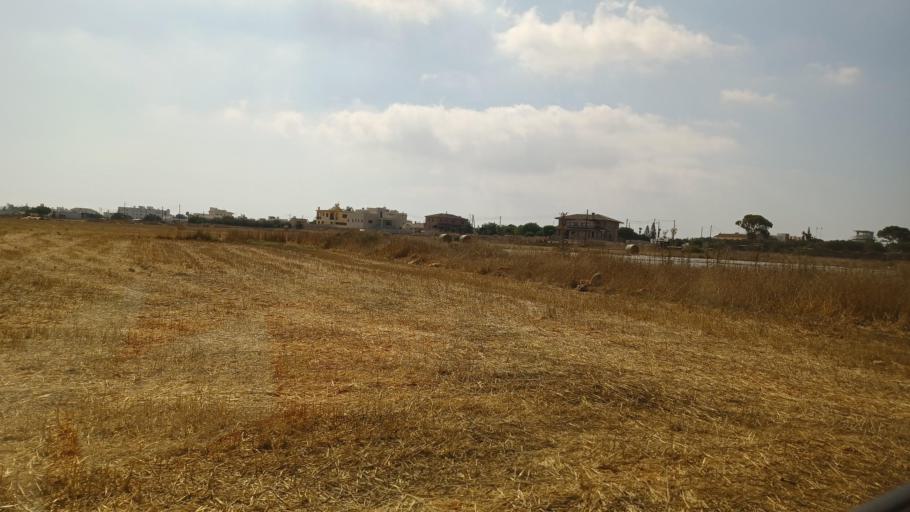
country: CY
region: Ammochostos
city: Deryneia
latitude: 35.0675
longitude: 33.9506
